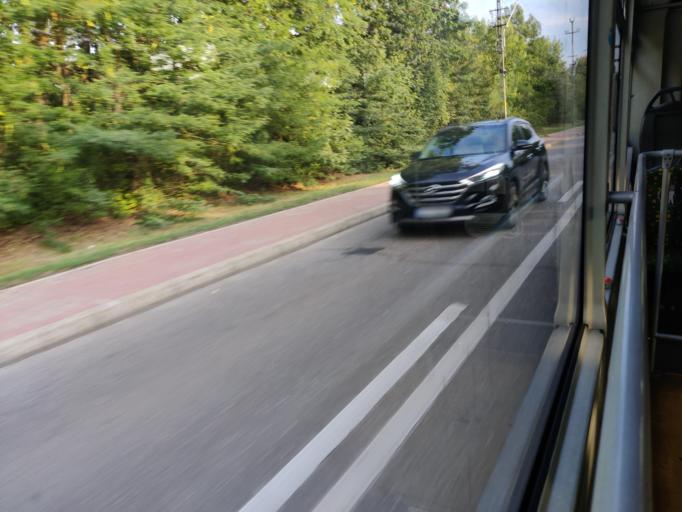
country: RO
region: Iasi
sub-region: Municipiul Iasi
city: Iasi
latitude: 47.1782
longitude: 27.5981
